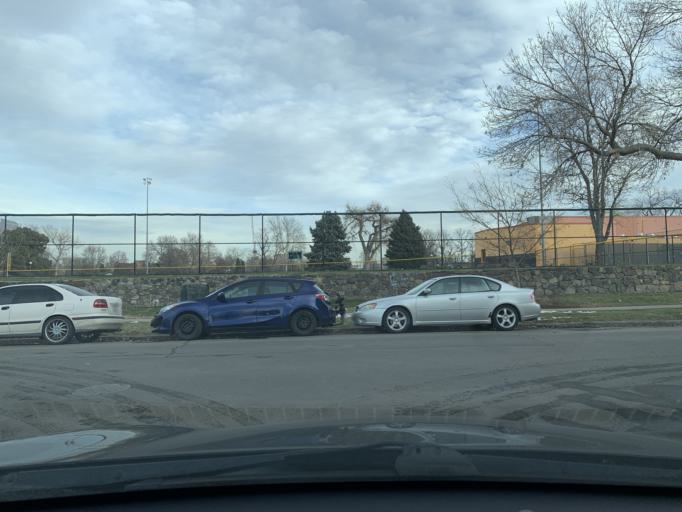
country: US
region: Colorado
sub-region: Denver County
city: Denver
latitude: 39.7353
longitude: -105.0055
